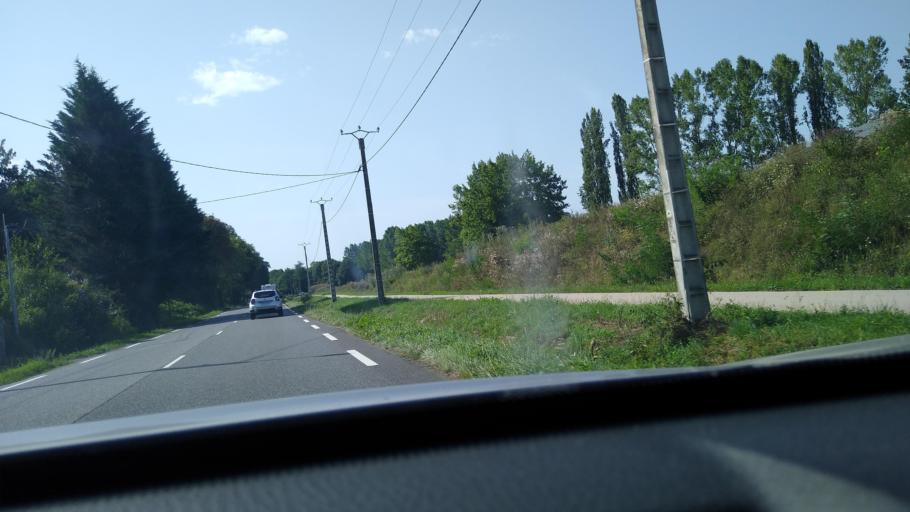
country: FR
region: Midi-Pyrenees
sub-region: Departement de la Haute-Garonne
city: Salies-du-Salat
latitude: 43.0744
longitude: 0.9625
